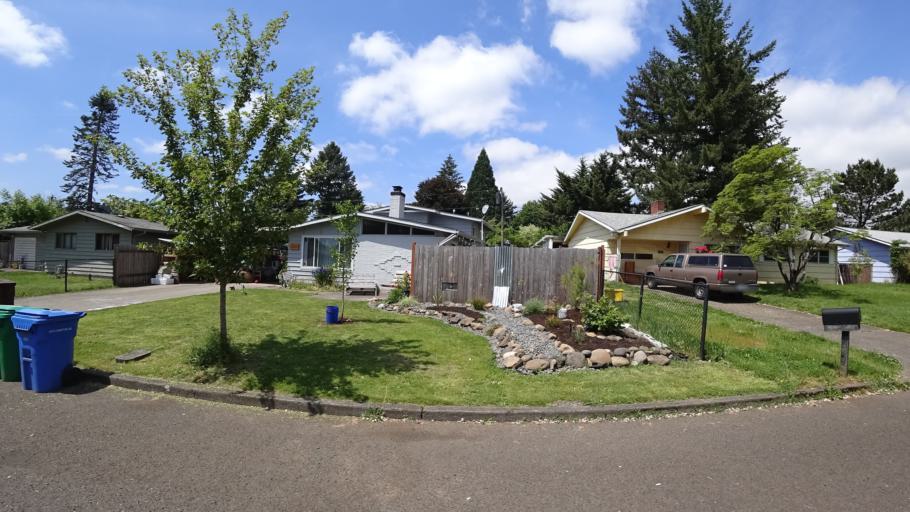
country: US
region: Oregon
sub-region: Multnomah County
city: Gresham
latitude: 45.4985
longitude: -122.4917
